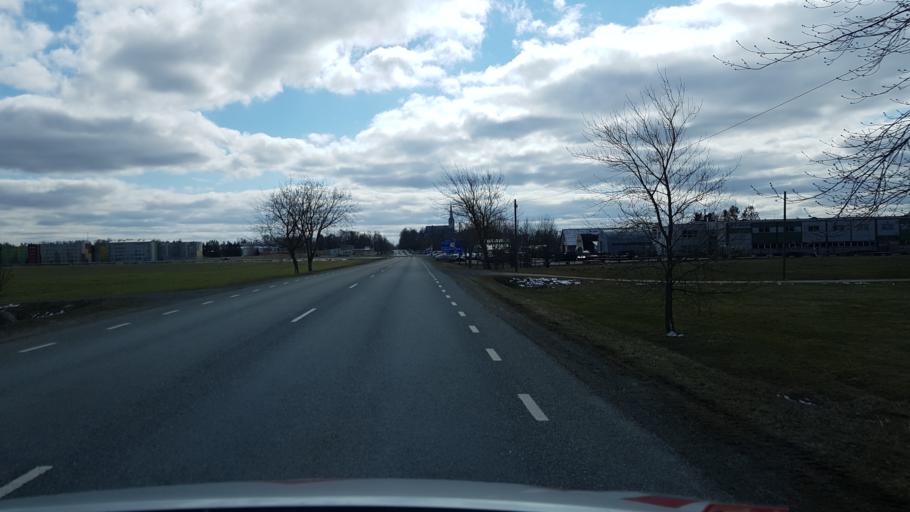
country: EE
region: Laeaene-Virumaa
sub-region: Kadrina vald
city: Kadrina
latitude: 59.3488
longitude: 26.1236
